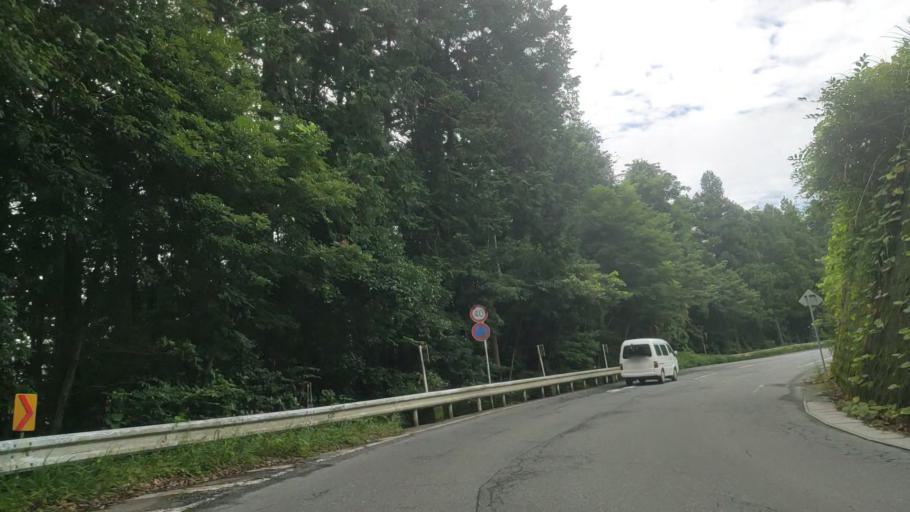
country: JP
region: Shizuoka
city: Fujinomiya
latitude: 35.2291
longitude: 138.5344
